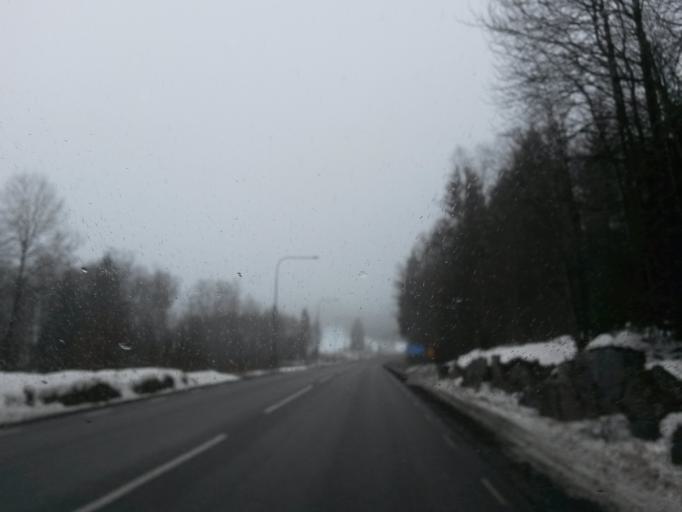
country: SE
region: Vaestra Goetaland
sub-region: Boras Kommun
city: Dalsjofors
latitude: 57.6978
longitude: 13.0570
